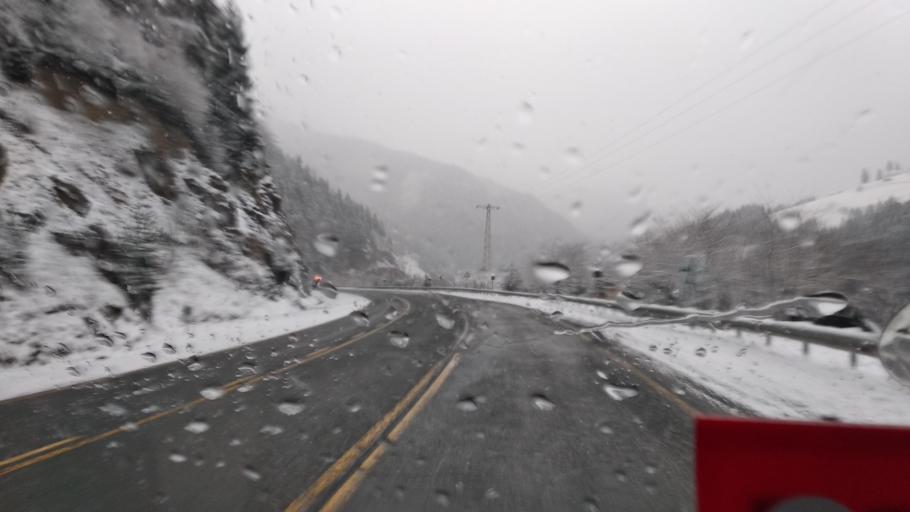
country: TR
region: Gumushane
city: Yaglidere
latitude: 40.6846
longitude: 39.4515
